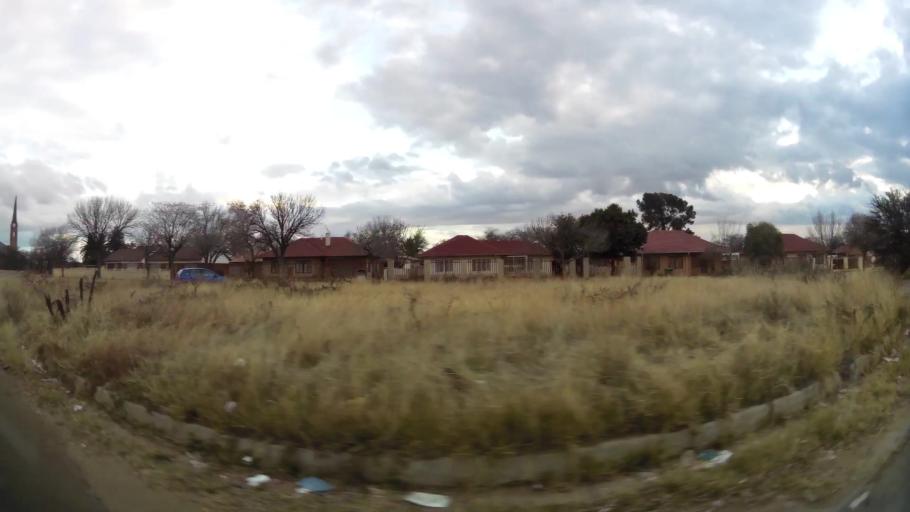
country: ZA
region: Orange Free State
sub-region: Lejweleputswa District Municipality
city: Welkom
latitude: -27.9684
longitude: 26.7679
